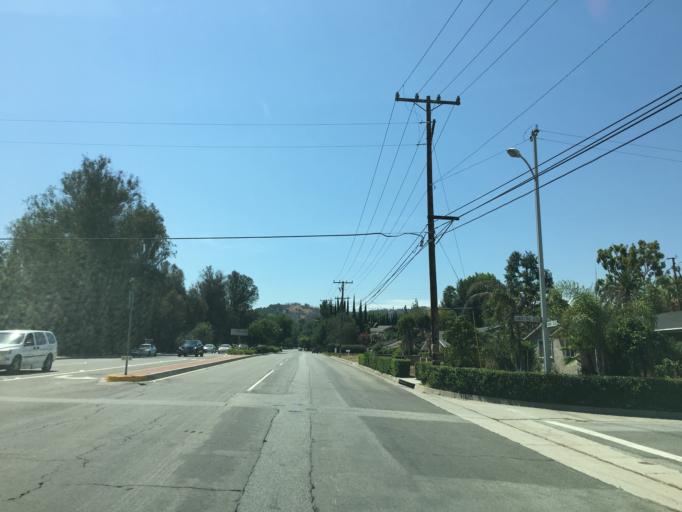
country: US
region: California
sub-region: Los Angeles County
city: Covina
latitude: 34.0669
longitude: -117.8706
